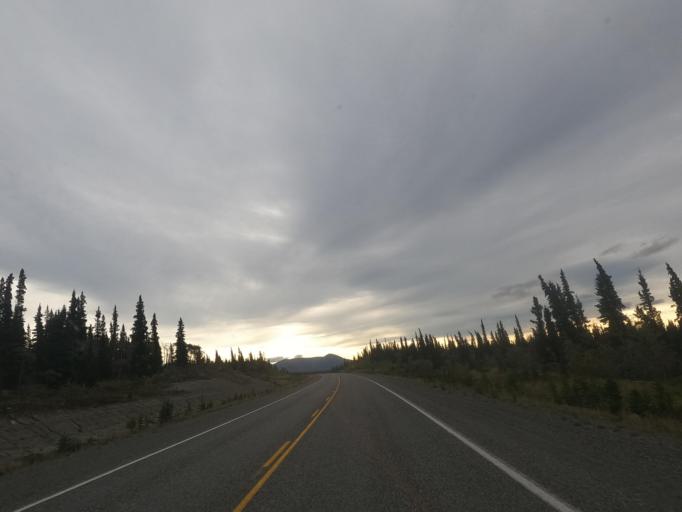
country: CA
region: Yukon
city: Haines Junction
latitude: 60.8073
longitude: -136.5356
